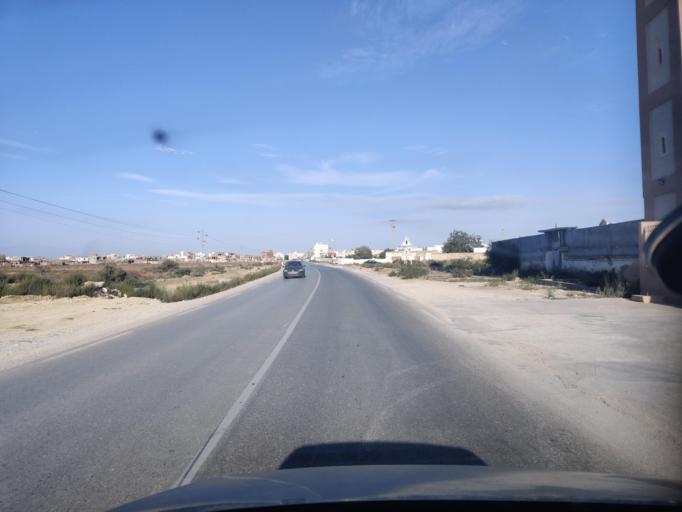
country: TN
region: Ariana
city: Ariana
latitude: 36.9543
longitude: 10.2308
